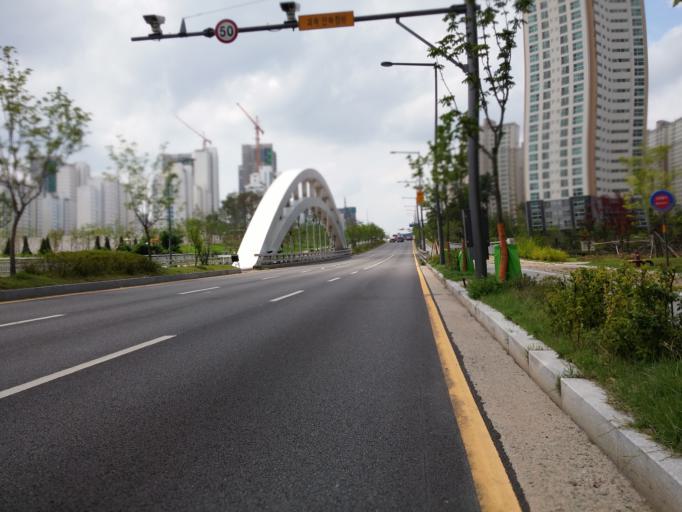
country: KR
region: Chungcheongnam-do
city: Gongju
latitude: 36.4990
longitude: 127.2527
